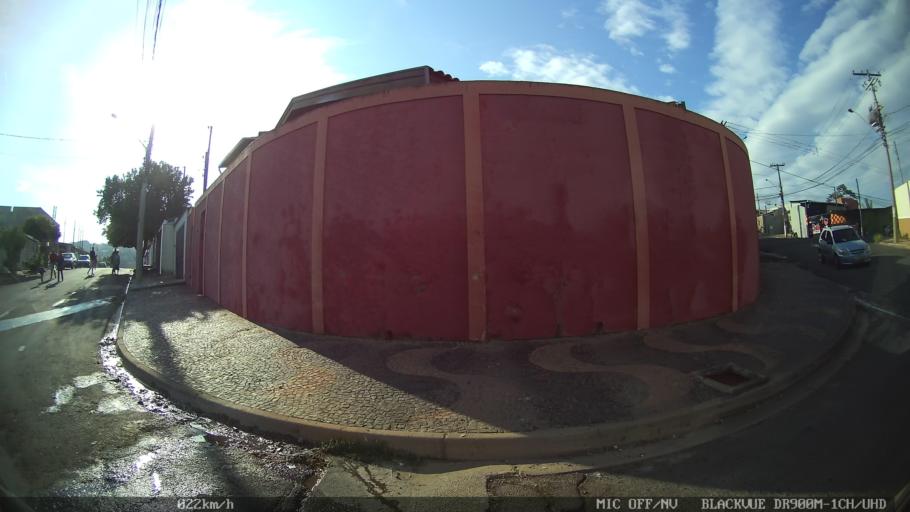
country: BR
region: Sao Paulo
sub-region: Santa Barbara D'Oeste
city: Santa Barbara d'Oeste
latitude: -22.7277
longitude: -47.3775
